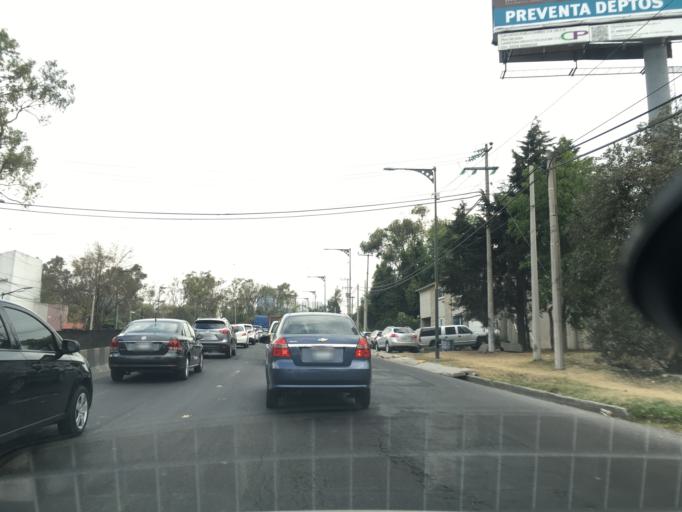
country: MX
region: Mexico City
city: Col. Bosques de las Lomas
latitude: 19.3723
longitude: -99.2702
